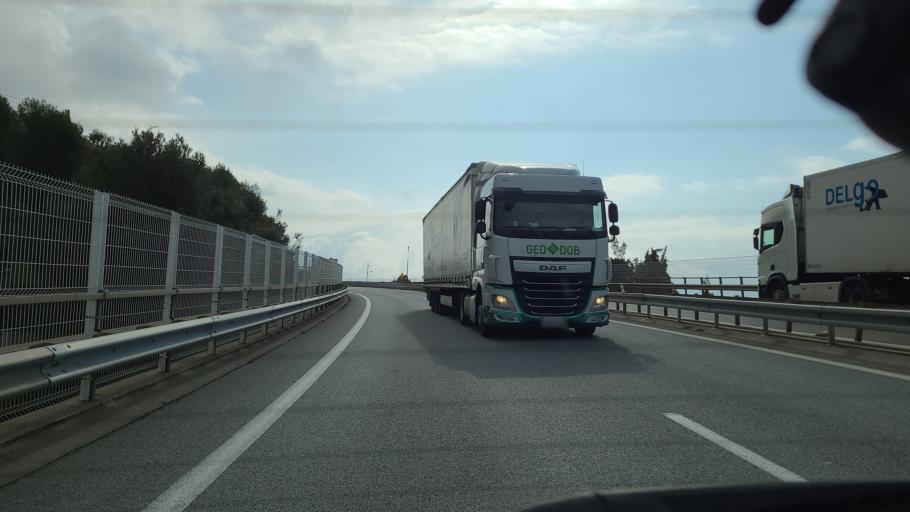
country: FR
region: Provence-Alpes-Cote d'Azur
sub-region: Departement des Alpes-Maritimes
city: Menton
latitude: 43.7914
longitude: 7.5159
